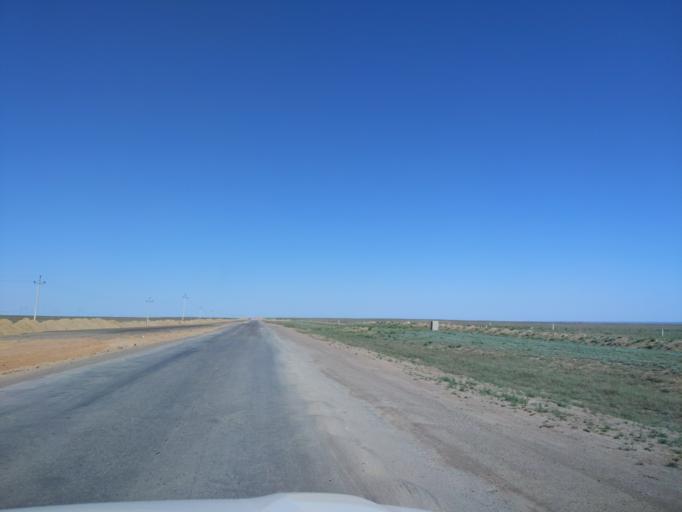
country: KZ
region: Almaty Oblysy
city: Bakanas
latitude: 44.1519
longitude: 75.8605
